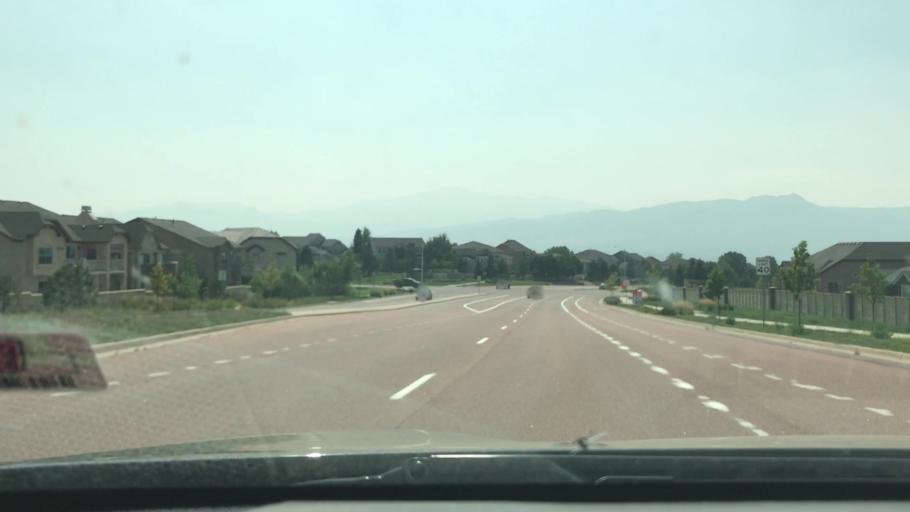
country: US
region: Colorado
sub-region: El Paso County
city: Black Forest
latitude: 38.9829
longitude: -104.7693
